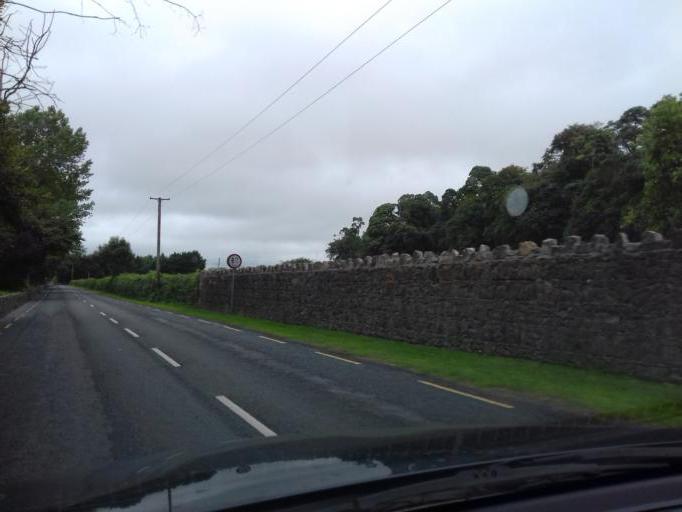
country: IE
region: Leinster
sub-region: County Carlow
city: Bagenalstown
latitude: 52.7125
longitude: -6.9562
